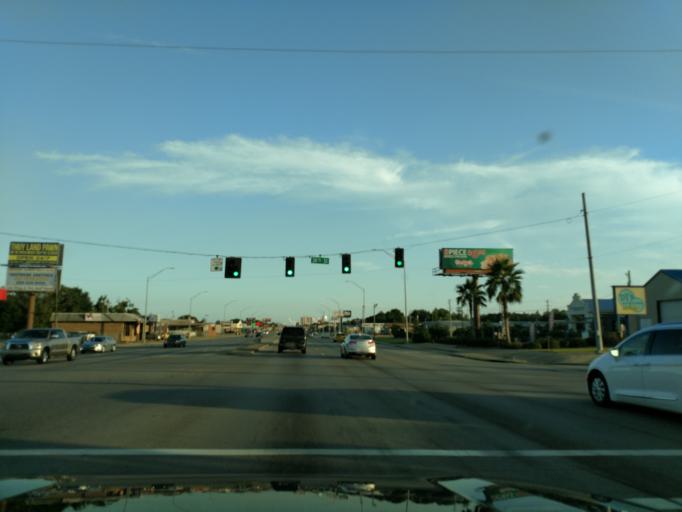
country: US
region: Mississippi
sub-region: Harrison County
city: West Gulfport
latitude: 30.3915
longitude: -89.0932
